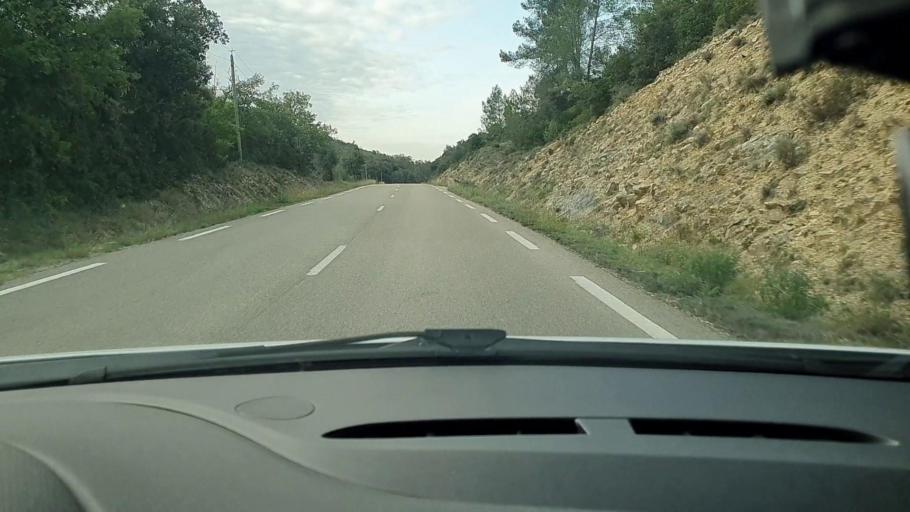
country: FR
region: Languedoc-Roussillon
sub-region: Departement du Gard
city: Mons
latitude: 44.1015
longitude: 4.2244
